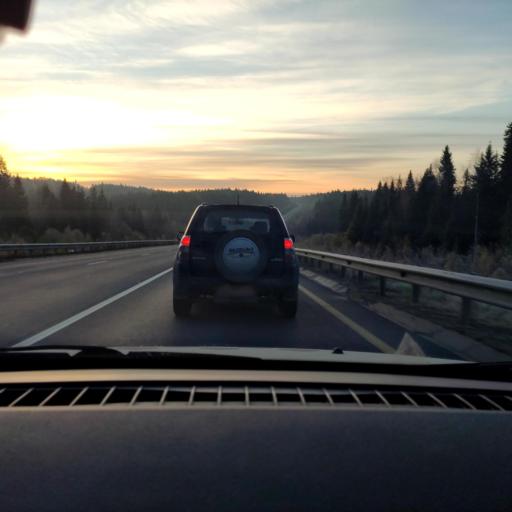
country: RU
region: Perm
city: Novyye Lyady
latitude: 58.0393
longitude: 56.4634
